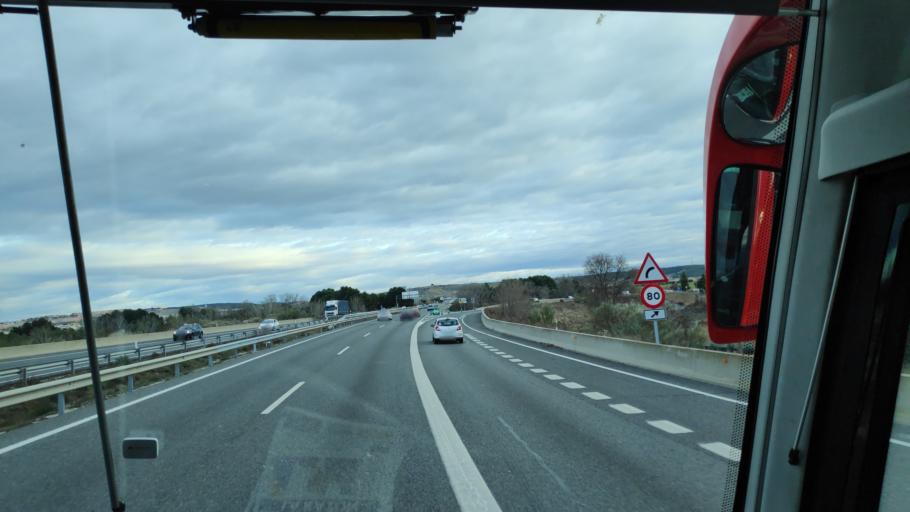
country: ES
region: Madrid
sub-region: Provincia de Madrid
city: Vaciamadrid
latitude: 40.3125
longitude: -3.4951
